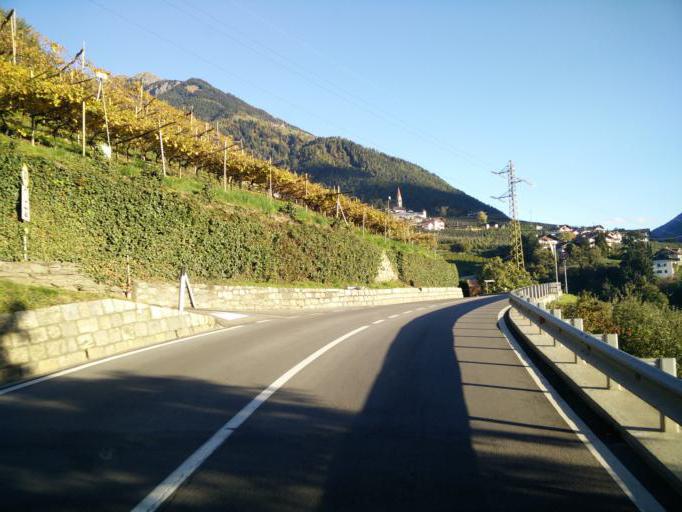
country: IT
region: Trentino-Alto Adige
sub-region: Bolzano
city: Caines
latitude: 46.6927
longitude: 11.1709
